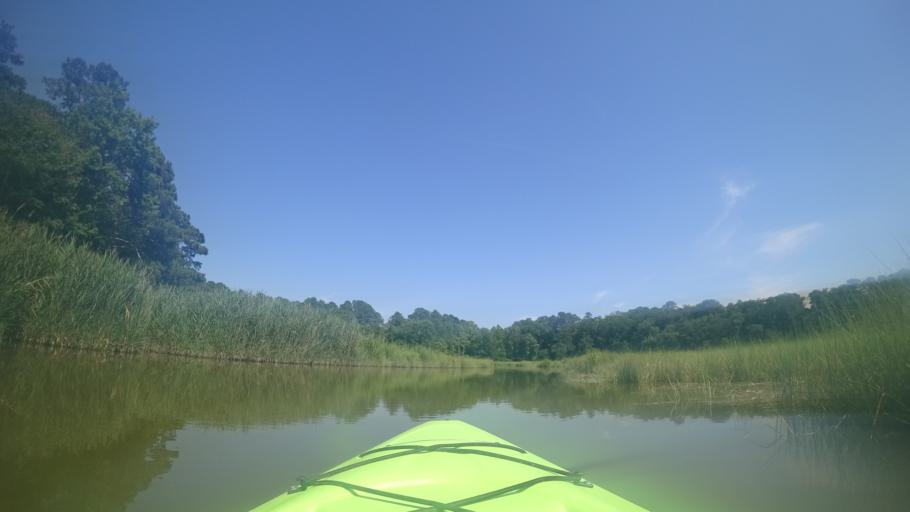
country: US
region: Virginia
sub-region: Isle of Wight County
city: Smithfield
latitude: 36.9565
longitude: -76.6144
